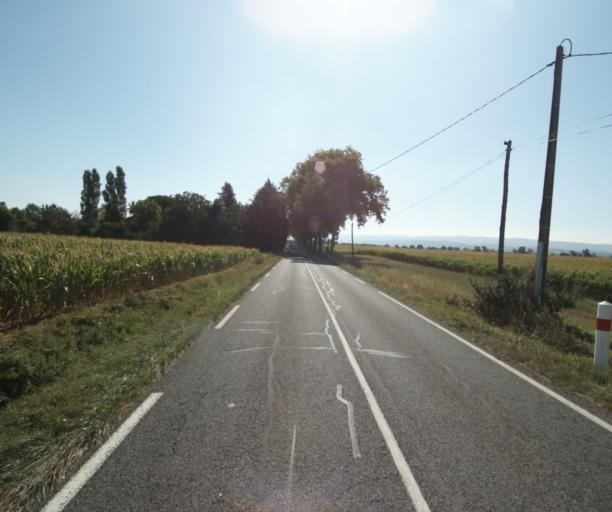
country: FR
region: Midi-Pyrenees
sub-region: Departement de la Haute-Garonne
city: Saint-Felix-Lauragais
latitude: 43.4736
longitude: 1.9403
